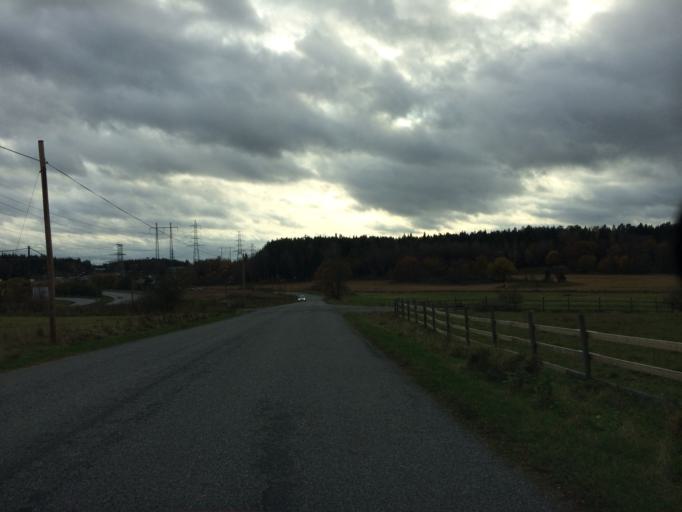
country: SE
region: Stockholm
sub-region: Sollentuna Kommun
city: Sollentuna
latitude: 59.4377
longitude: 17.9219
